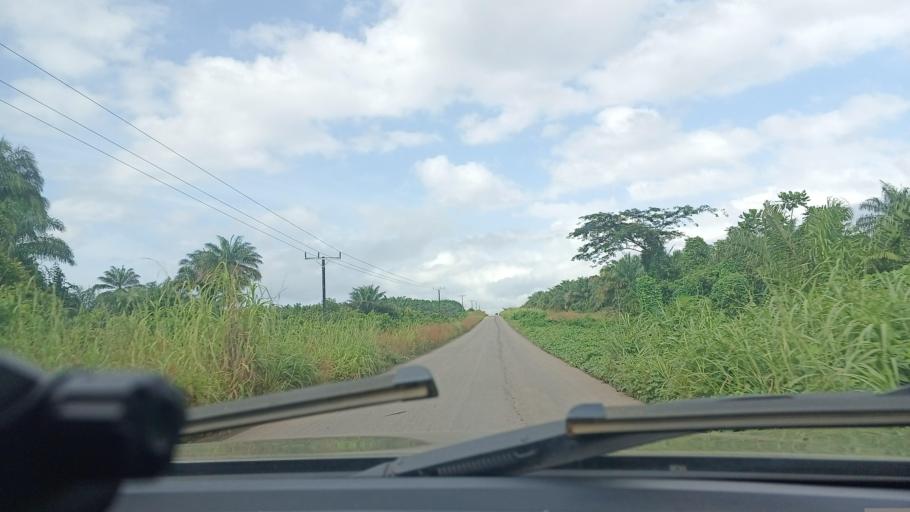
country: LR
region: Bomi
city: Tubmanburg
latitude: 6.7287
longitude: -11.0250
